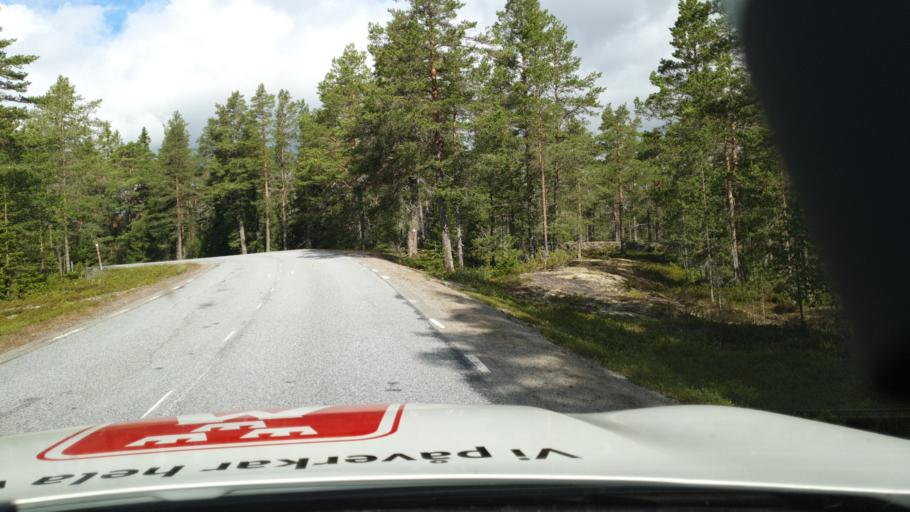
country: SE
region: Vaesterbotten
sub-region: Umea Kommun
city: Roback
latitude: 63.6766
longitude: 20.0857
